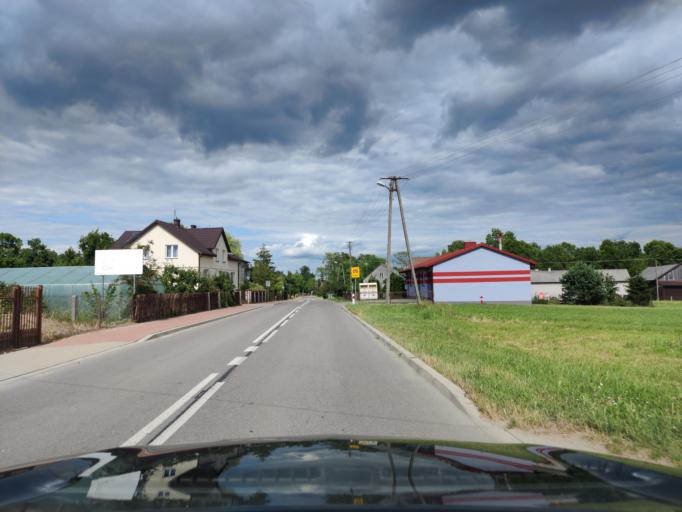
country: PL
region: Masovian Voivodeship
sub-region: Powiat sokolowski
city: Ceranow
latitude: 52.6115
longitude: 22.1996
